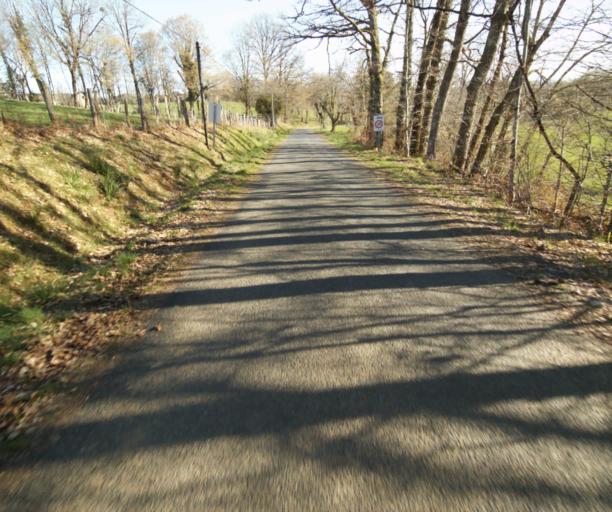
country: FR
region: Limousin
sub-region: Departement de la Correze
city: Seilhac
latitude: 45.3706
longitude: 1.7487
